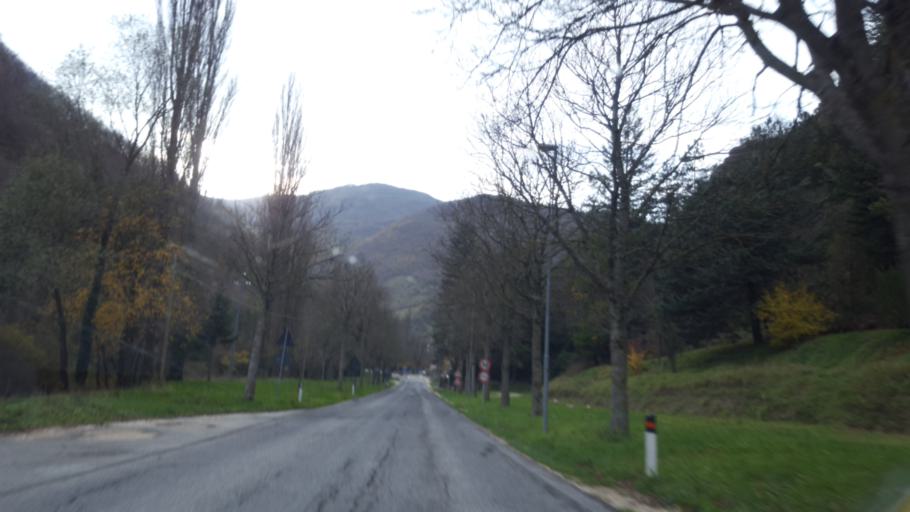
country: IT
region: The Marches
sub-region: Provincia di Macerata
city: Visso
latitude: 42.9330
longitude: 13.0937
